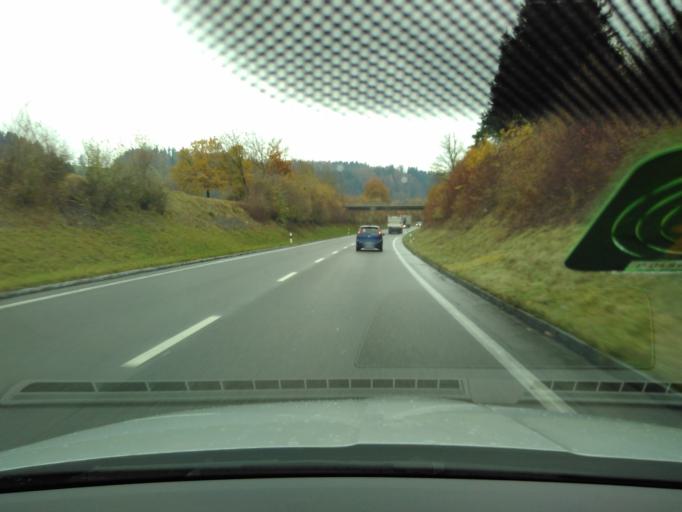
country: CH
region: Aargau
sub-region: Bezirk Kulm
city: Schoftland
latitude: 47.2993
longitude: 8.0443
